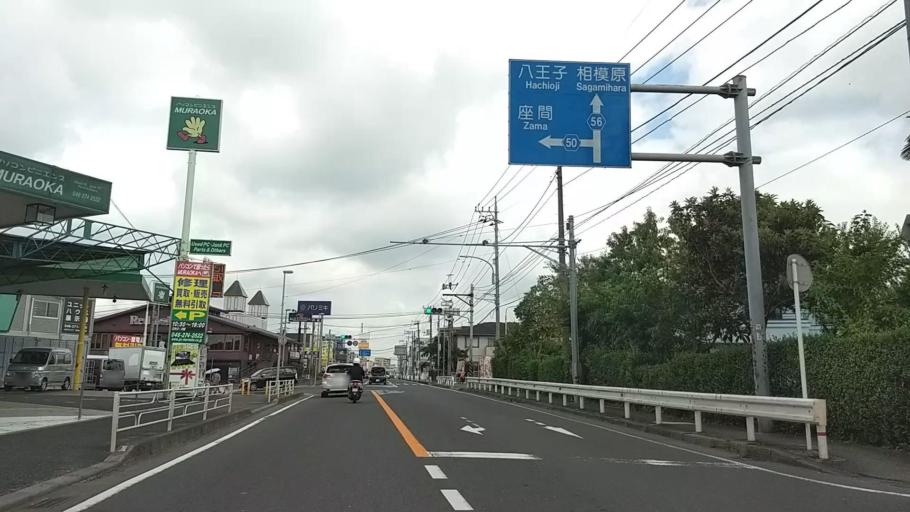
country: JP
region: Kanagawa
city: Minami-rinkan
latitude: 35.5041
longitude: 139.4647
